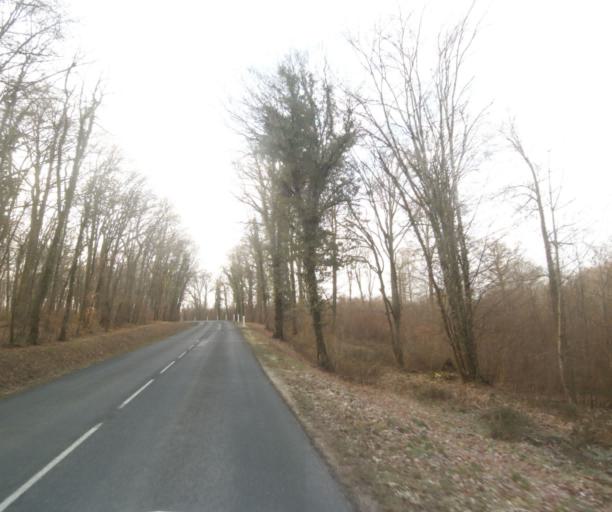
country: FR
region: Champagne-Ardenne
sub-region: Departement de la Marne
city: Sermaize-les-Bains
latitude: 48.7544
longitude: 4.9007
